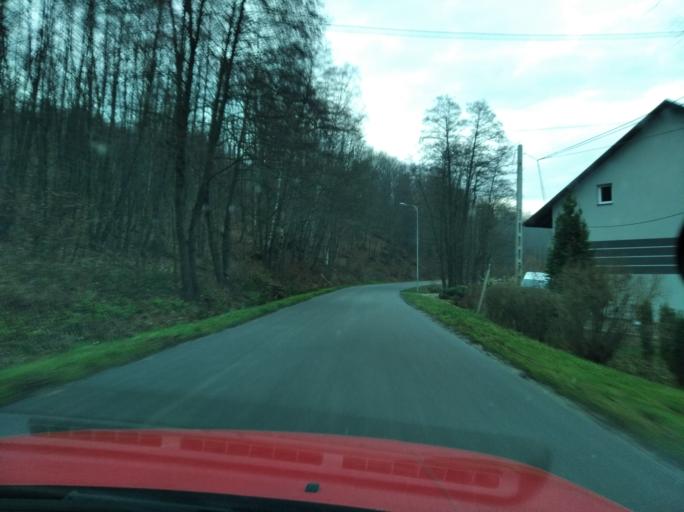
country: PL
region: Subcarpathian Voivodeship
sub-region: Powiat strzyzowski
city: Niebylec
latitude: 49.8661
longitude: 21.8868
